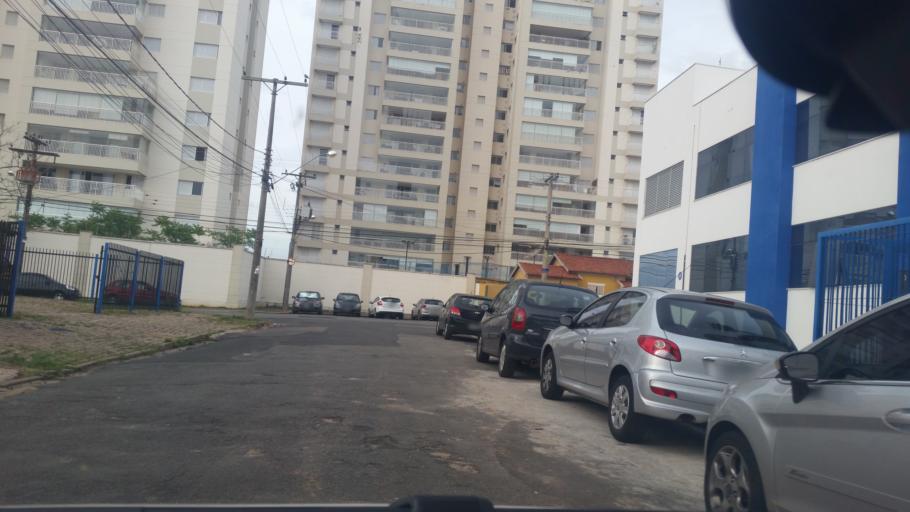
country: BR
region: Sao Paulo
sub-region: Campinas
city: Campinas
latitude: -22.8840
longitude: -47.0612
